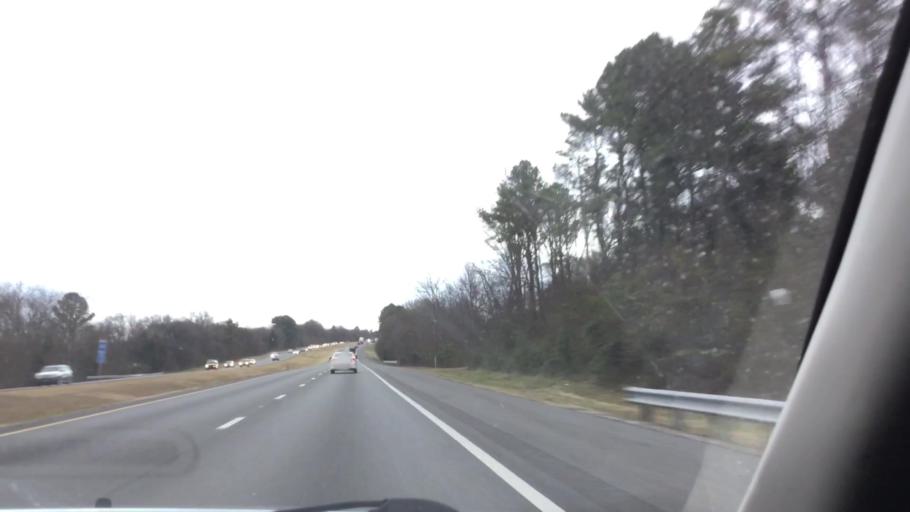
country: US
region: Tennessee
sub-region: Williamson County
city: Thompson's Station
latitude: 35.7751
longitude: -86.8637
